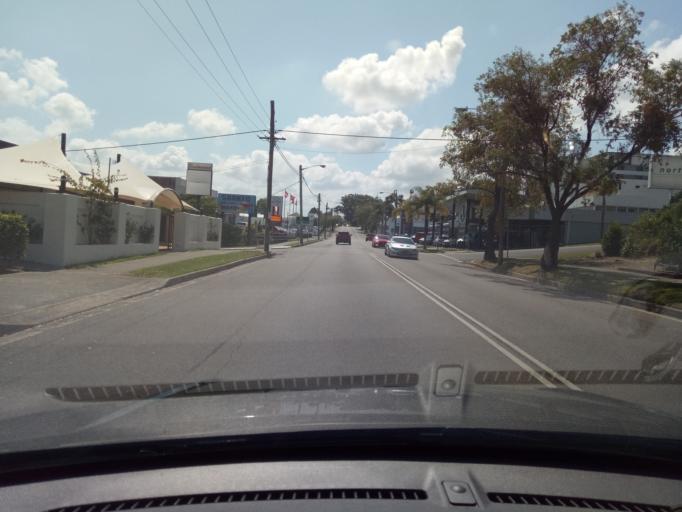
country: AU
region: New South Wales
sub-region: Gosford Shire
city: Gosford
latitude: -33.4175
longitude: 151.3439
